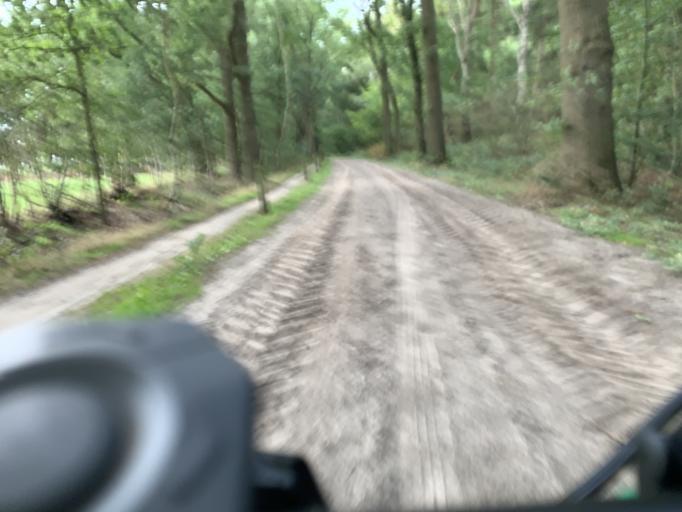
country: DE
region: Lower Saxony
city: Westerstede
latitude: 53.2326
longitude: 7.9185
